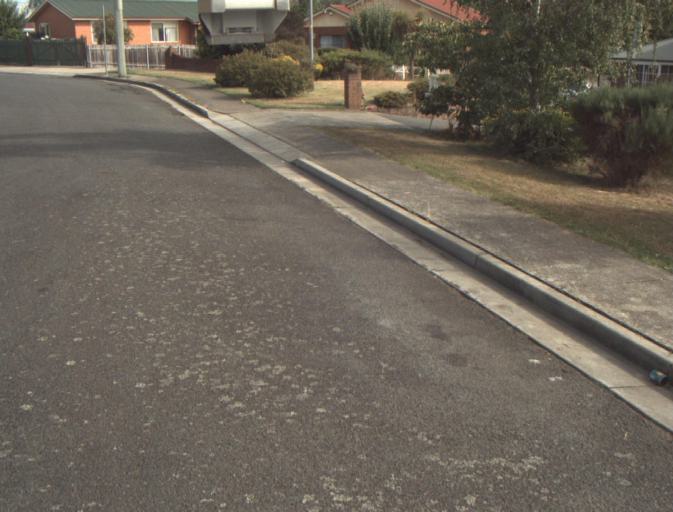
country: AU
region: Tasmania
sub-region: Launceston
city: Invermay
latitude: -41.3903
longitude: 147.1365
